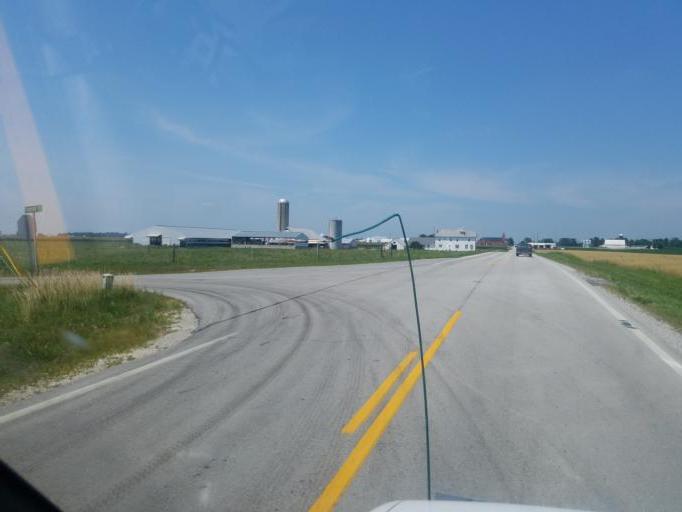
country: US
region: Ohio
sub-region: Auglaize County
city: Minster
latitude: 40.3781
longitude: -84.4340
